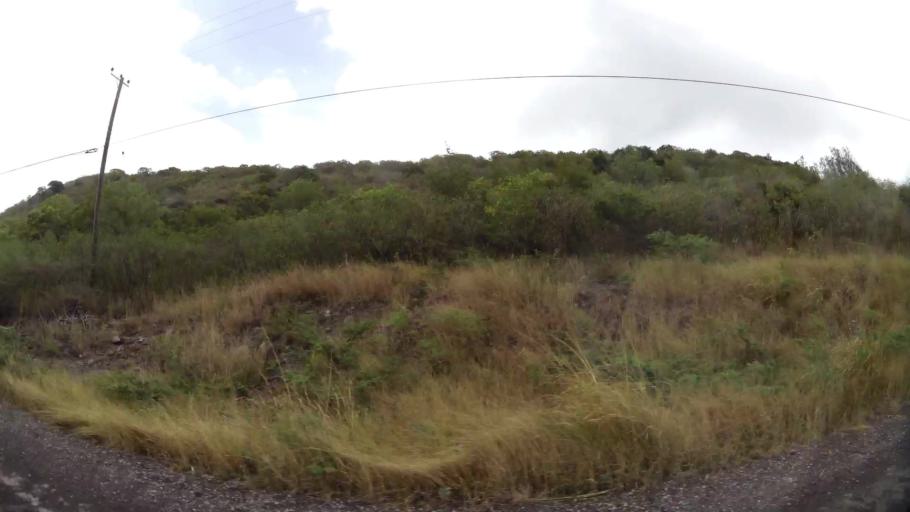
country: KN
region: Saint James Windwa
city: Newcastle
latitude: 17.2029
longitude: -62.6082
